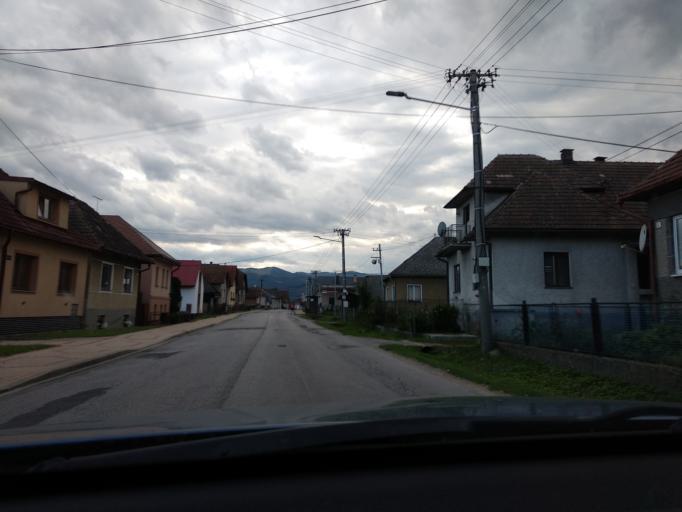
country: SK
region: Zilinsky
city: Ruzomberok
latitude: 49.0920
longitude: 19.3599
